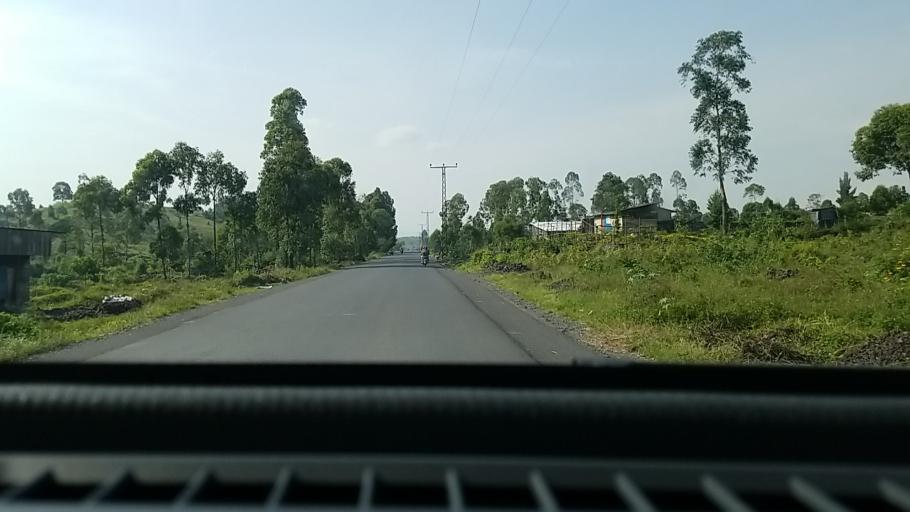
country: CD
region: Nord Kivu
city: Goma
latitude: -1.6141
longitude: 29.1426
